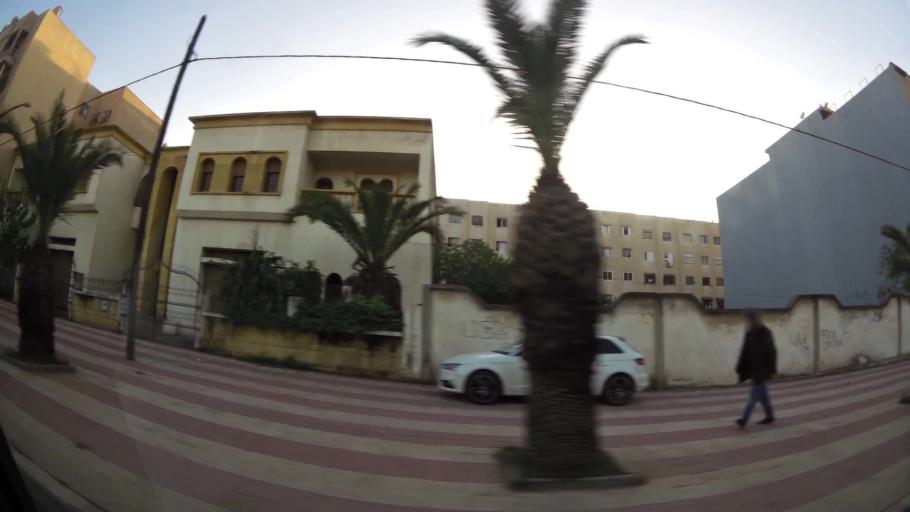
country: MA
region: Chaouia-Ouardigha
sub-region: Settat Province
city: Settat
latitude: 32.9926
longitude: -7.6209
